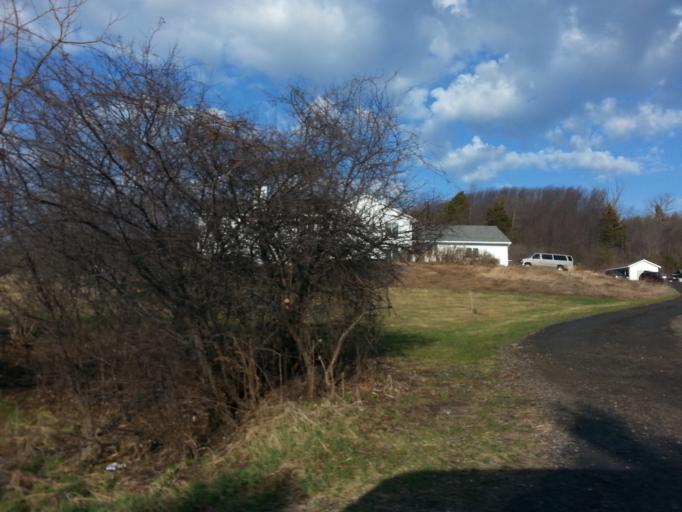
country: US
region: Minnesota
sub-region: Washington County
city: Afton
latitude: 44.8877
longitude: -92.8428
